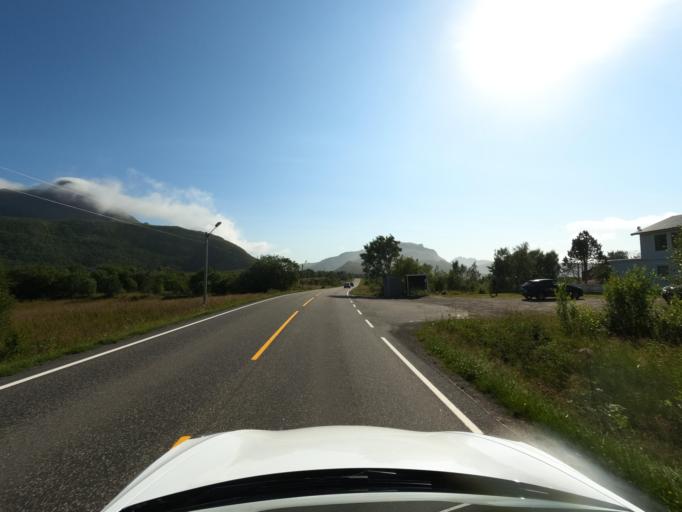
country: NO
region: Nordland
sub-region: Vestvagoy
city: Evjen
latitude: 68.2713
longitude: 14.0559
